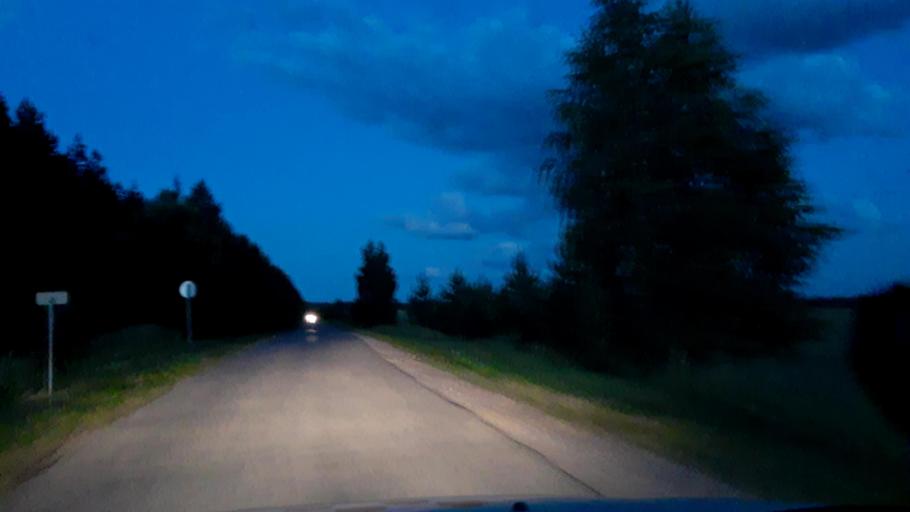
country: RU
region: Nizjnij Novgorod
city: Pamyat' Parizhskoy Kommuny
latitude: 56.0624
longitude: 44.4652
